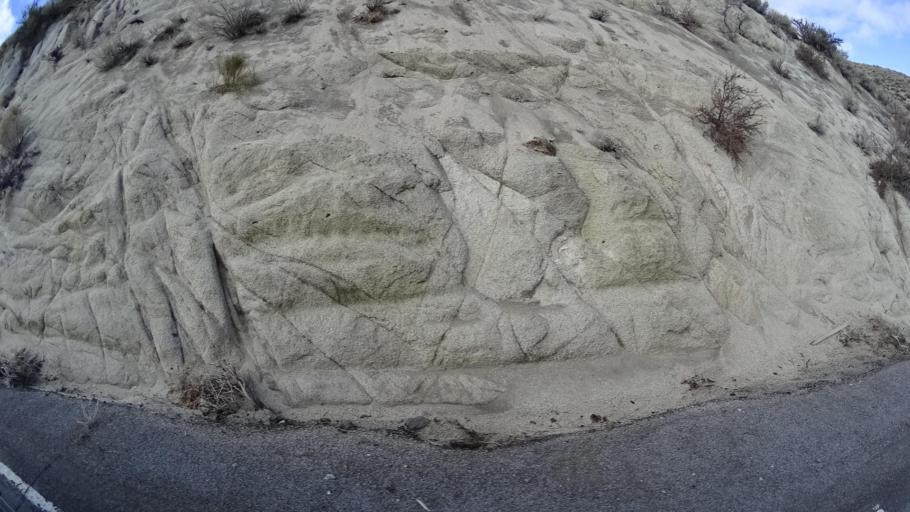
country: US
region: Nevada
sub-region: Washoe County
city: Cold Springs
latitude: 39.8212
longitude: -119.9370
